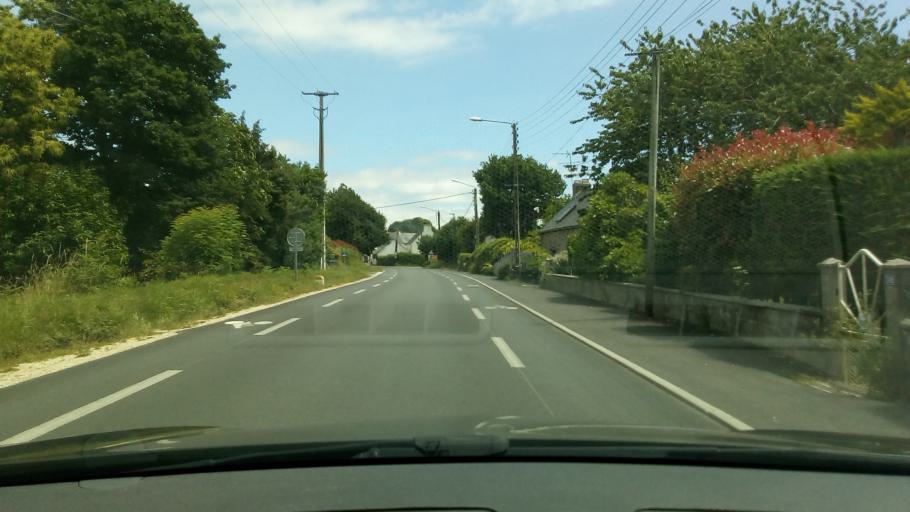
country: FR
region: Brittany
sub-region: Departement du Finistere
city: Tregunc
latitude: 47.8789
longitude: -3.8518
